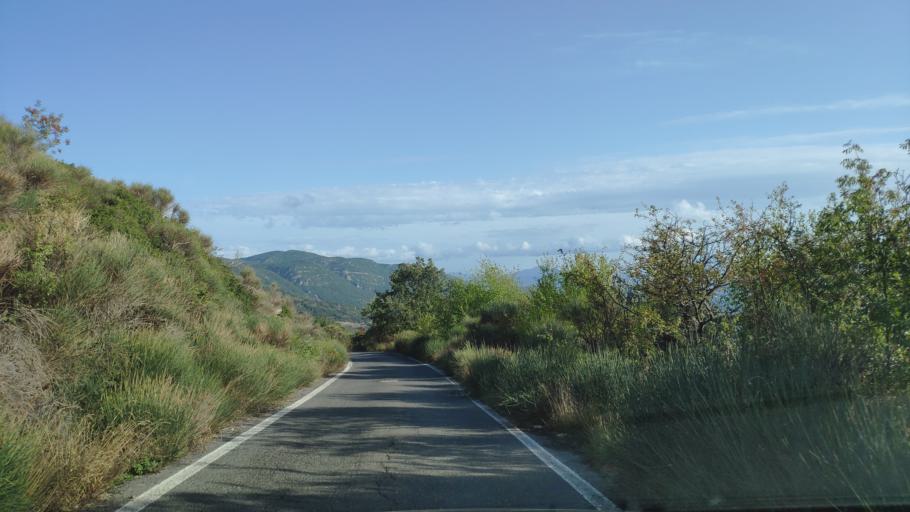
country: GR
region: Peloponnese
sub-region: Nomos Arkadias
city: Dimitsana
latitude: 37.5622
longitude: 22.0310
